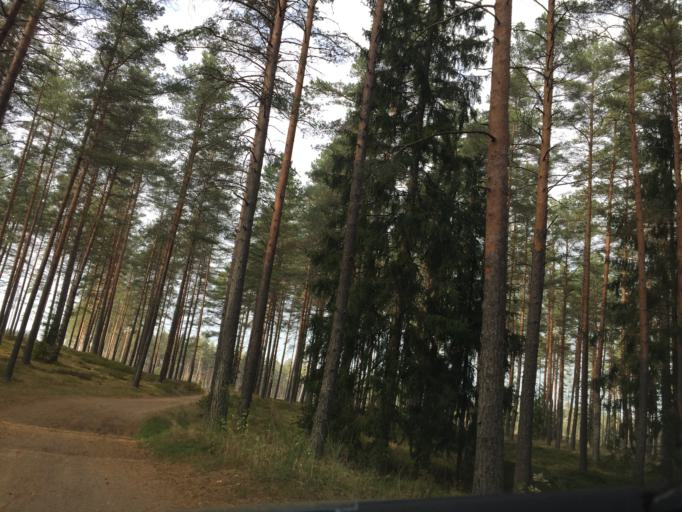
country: LV
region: Garkalne
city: Garkalne
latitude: 56.9529
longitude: 24.4249
